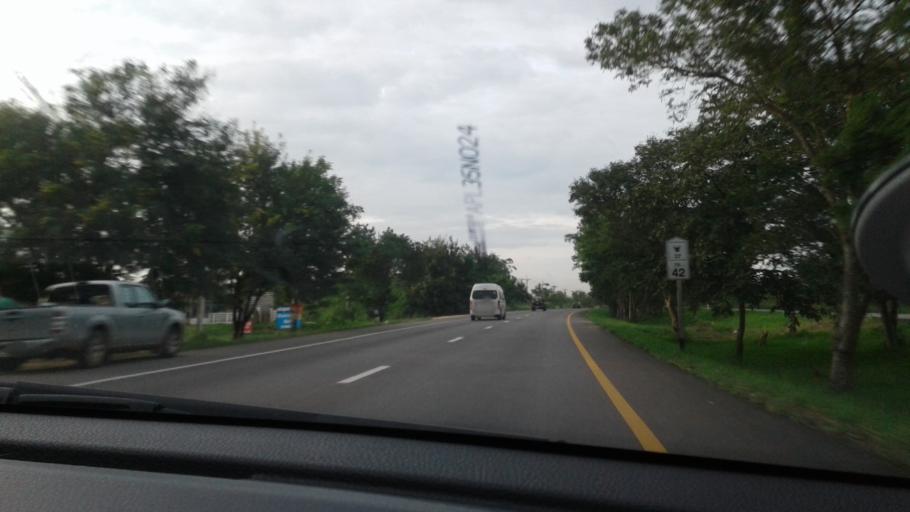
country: TH
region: Prachuap Khiri Khan
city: Pran Buri
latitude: 12.4604
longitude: 99.8984
